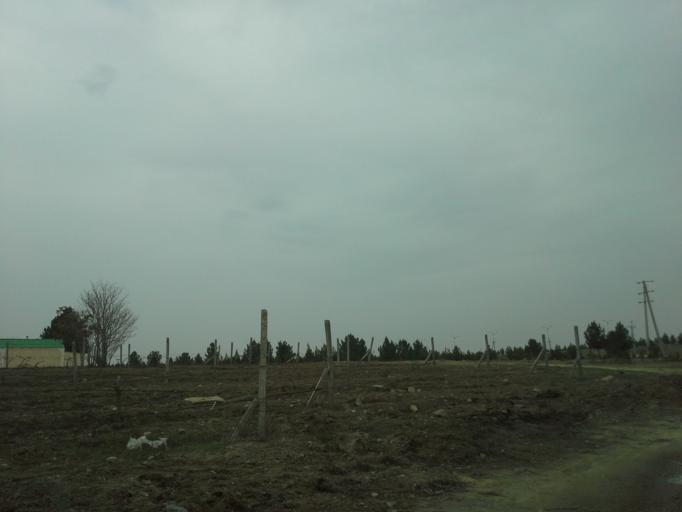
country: TM
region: Ahal
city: Abadan
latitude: 37.9812
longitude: 58.2262
